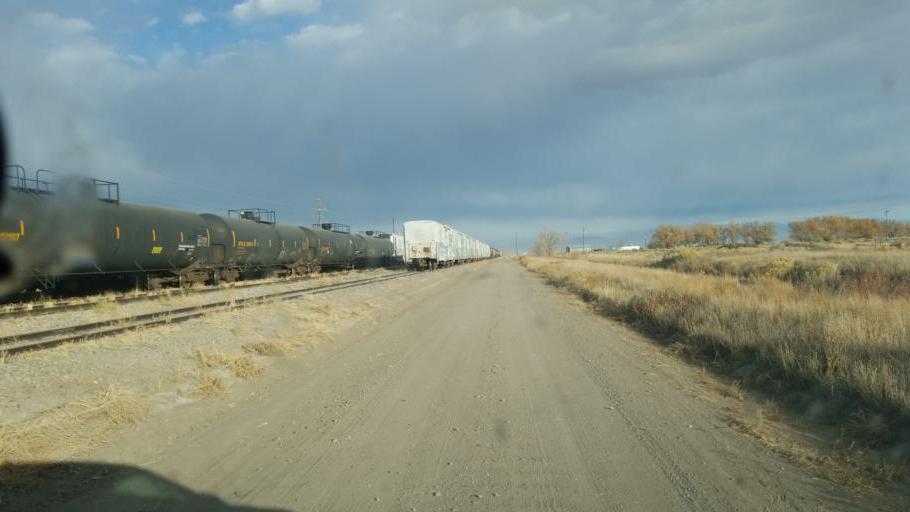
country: US
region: Colorado
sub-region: Alamosa County
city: Alamosa East
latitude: 37.4660
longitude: -105.8436
